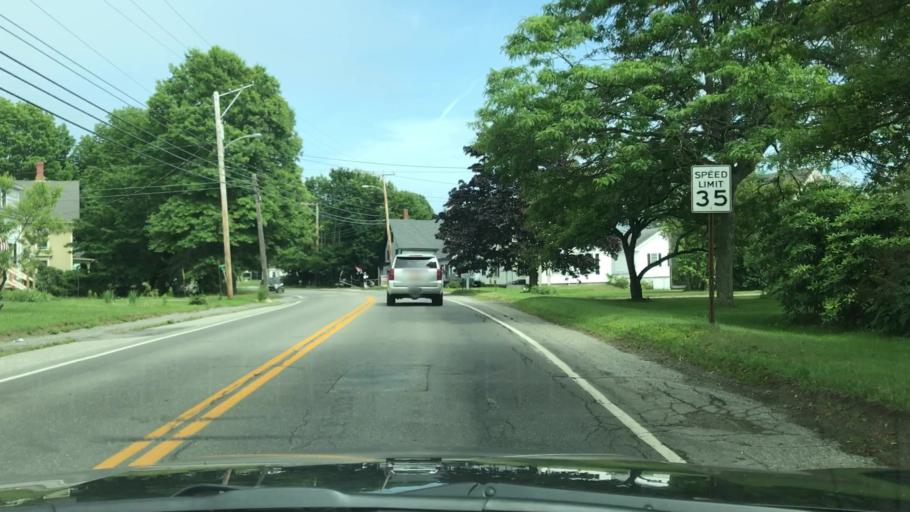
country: US
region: Maine
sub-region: Waldo County
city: Stockton Springs
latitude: 44.4578
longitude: -68.9179
